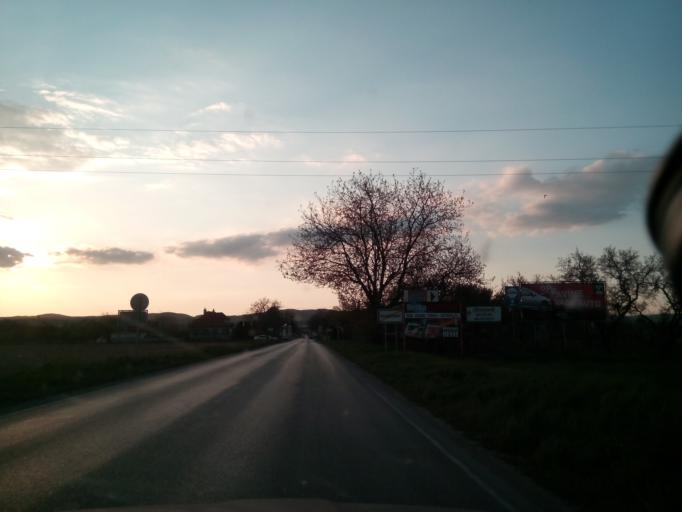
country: SK
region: Trnavsky
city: Vrbove
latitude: 48.6124
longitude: 17.7392
